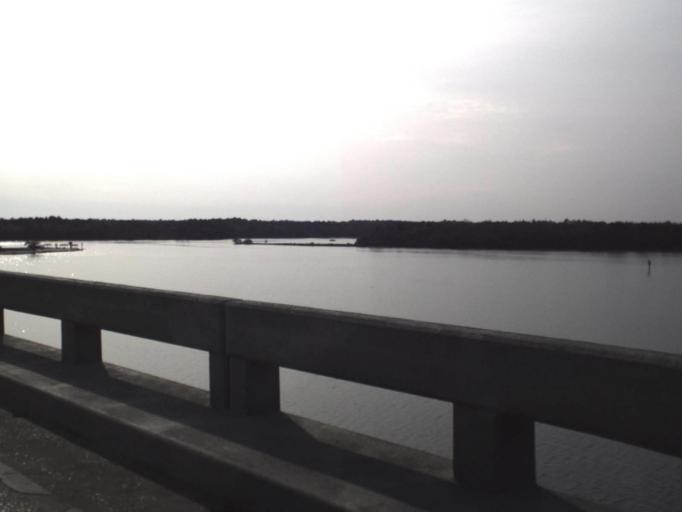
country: US
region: Florida
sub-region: Bay County
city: Tyndall Air Force Base
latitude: 30.1045
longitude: -85.6084
